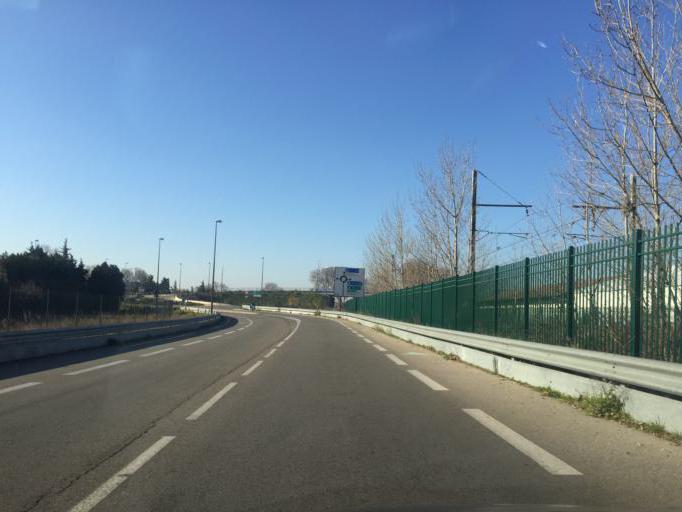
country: FR
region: Provence-Alpes-Cote d'Azur
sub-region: Departement du Vaucluse
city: Montfavet
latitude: 43.9324
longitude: 4.8501
